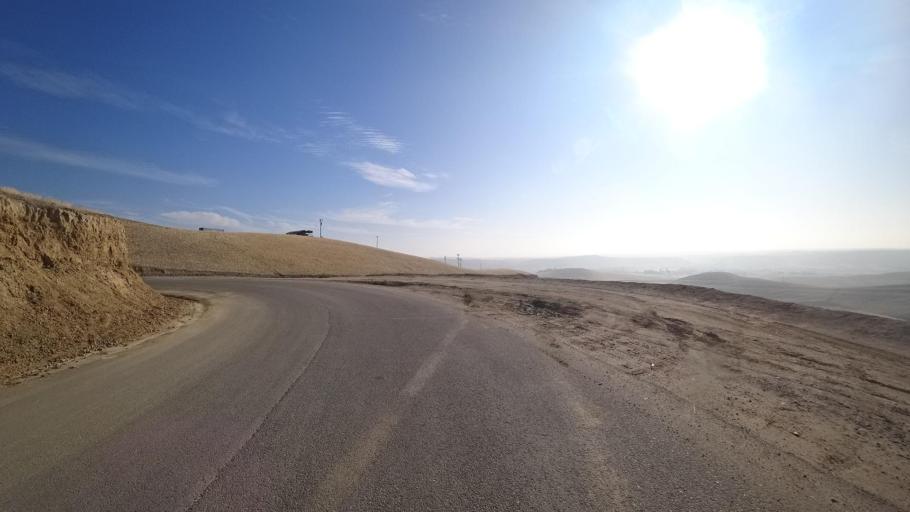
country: US
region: California
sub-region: Kern County
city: Oildale
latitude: 35.4611
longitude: -118.8720
